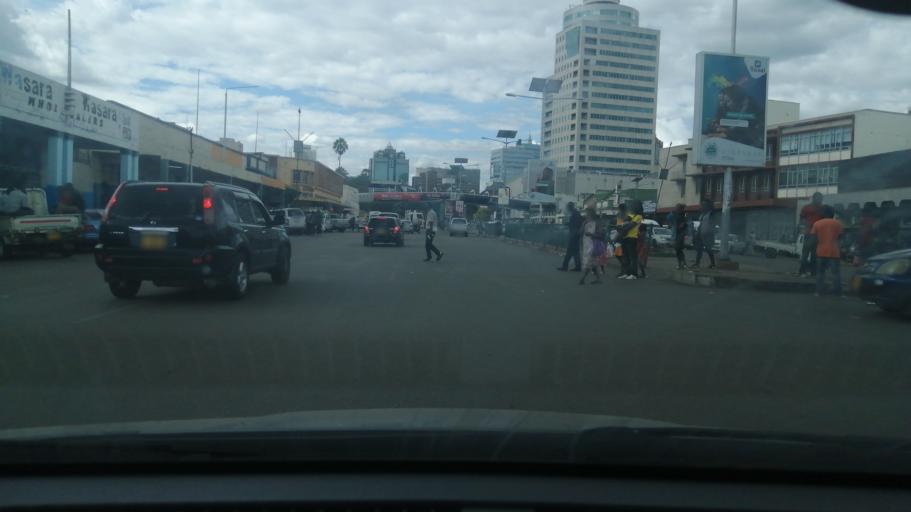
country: ZW
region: Harare
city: Harare
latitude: -17.8341
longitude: 31.0466
